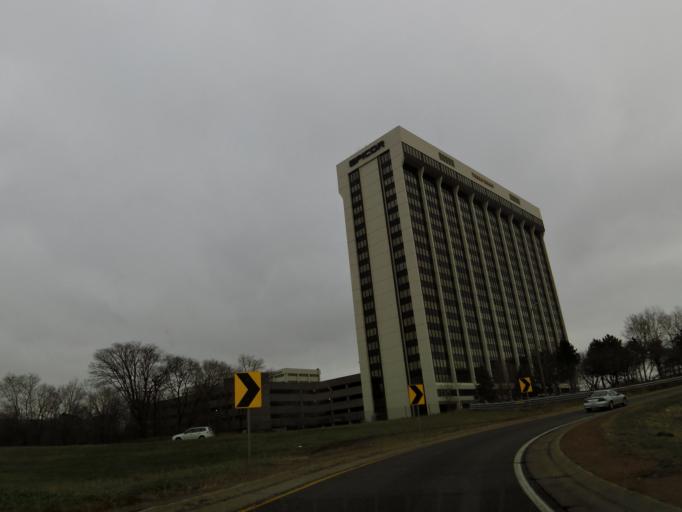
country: US
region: Minnesota
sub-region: Hennepin County
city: Minnetonka Mills
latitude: 44.9738
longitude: -93.4020
